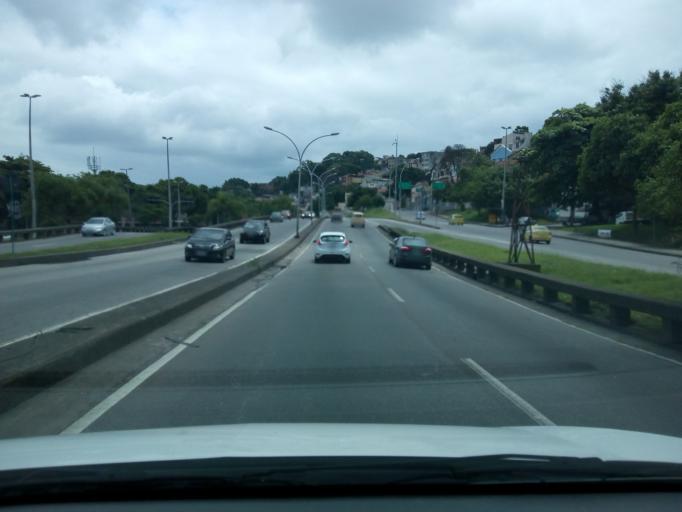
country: BR
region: Rio de Janeiro
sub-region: Rio De Janeiro
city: Rio de Janeiro
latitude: -22.9182
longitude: -43.1945
